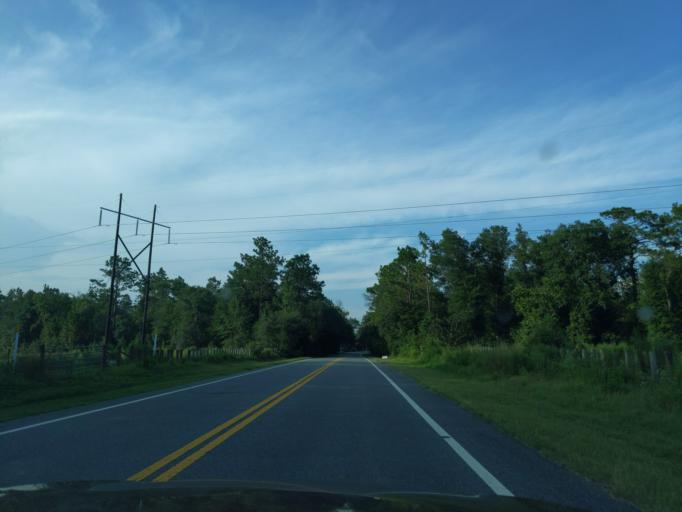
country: US
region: Florida
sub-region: Leon County
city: Tallahassee
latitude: 30.3701
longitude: -84.3626
